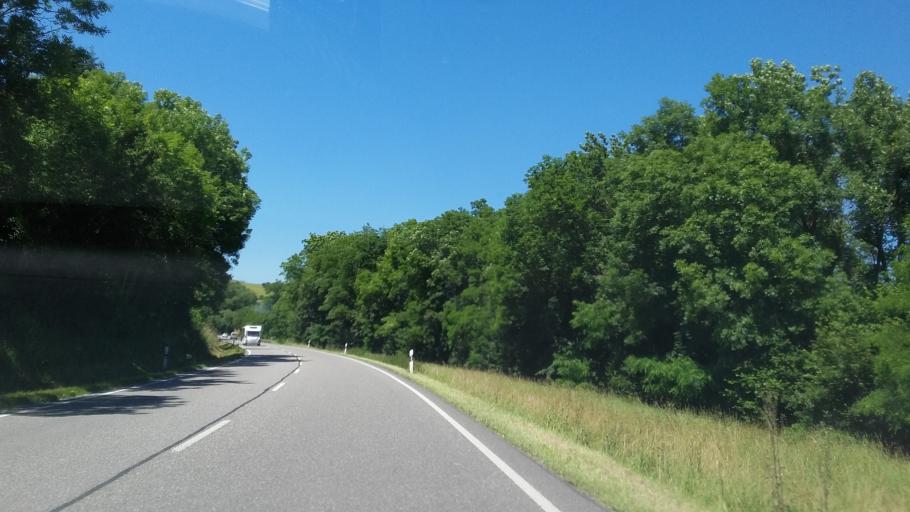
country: DE
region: Baden-Wuerttemberg
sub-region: Regierungsbezirk Stuttgart
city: Vaihingen an der Enz
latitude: 48.9330
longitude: 8.9480
